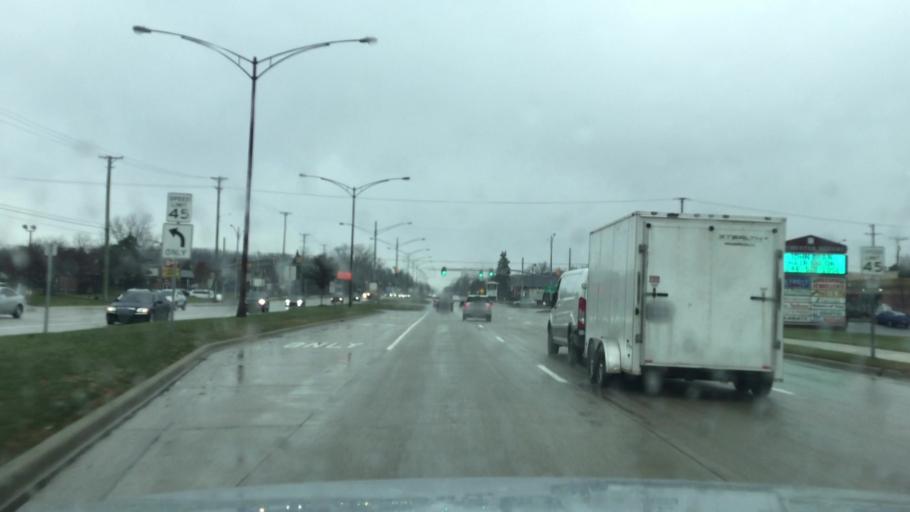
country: US
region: Michigan
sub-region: Oakland County
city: Troy
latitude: 42.5763
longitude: -83.1282
